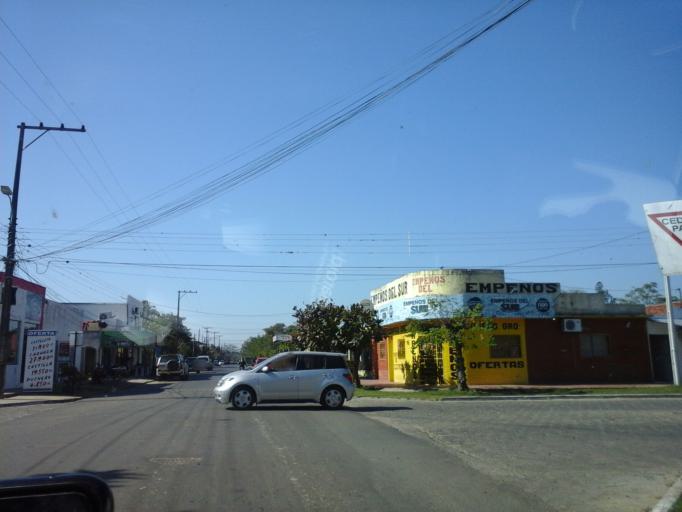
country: PY
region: Neembucu
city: Pilar
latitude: -26.8629
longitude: -58.3033
